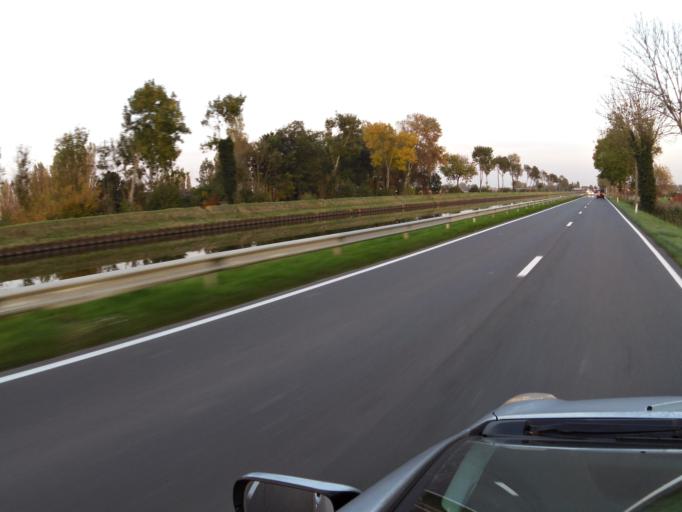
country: BE
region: Flanders
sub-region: Provincie West-Vlaanderen
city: Ostend
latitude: 51.1727
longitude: 2.9020
